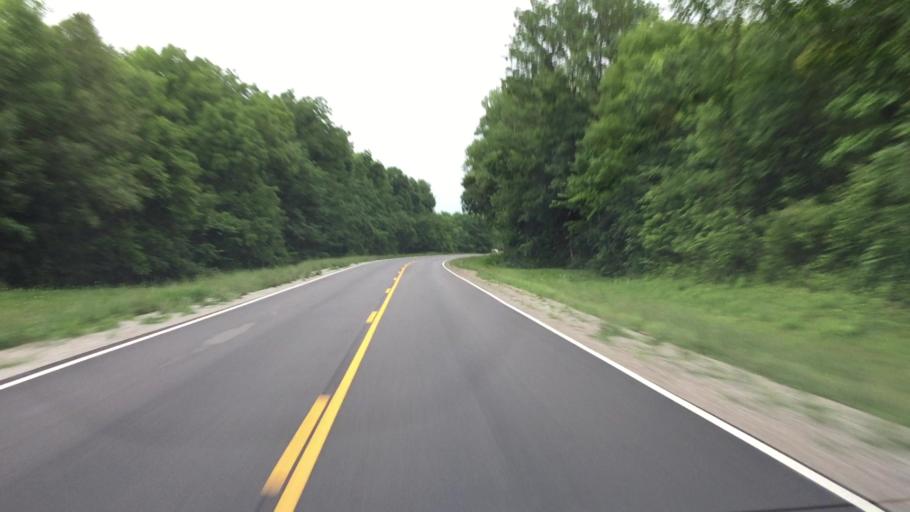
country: US
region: Iowa
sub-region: Lee County
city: Keokuk
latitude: 40.3729
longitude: -91.3914
